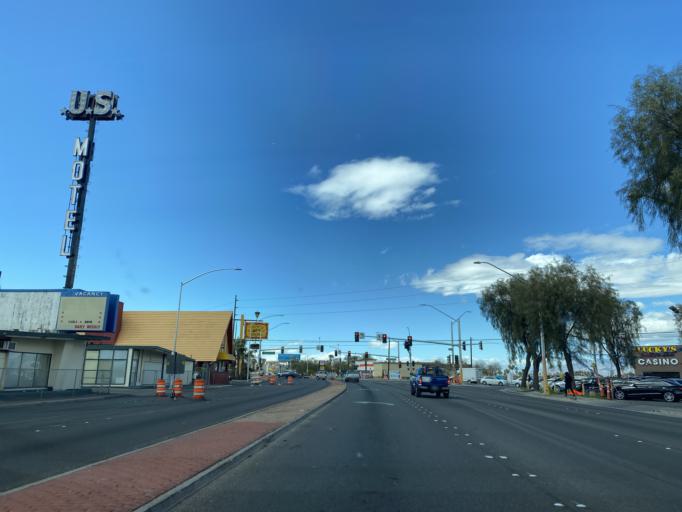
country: US
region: Nevada
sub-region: Clark County
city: Las Vegas
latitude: 36.1581
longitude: -115.1156
